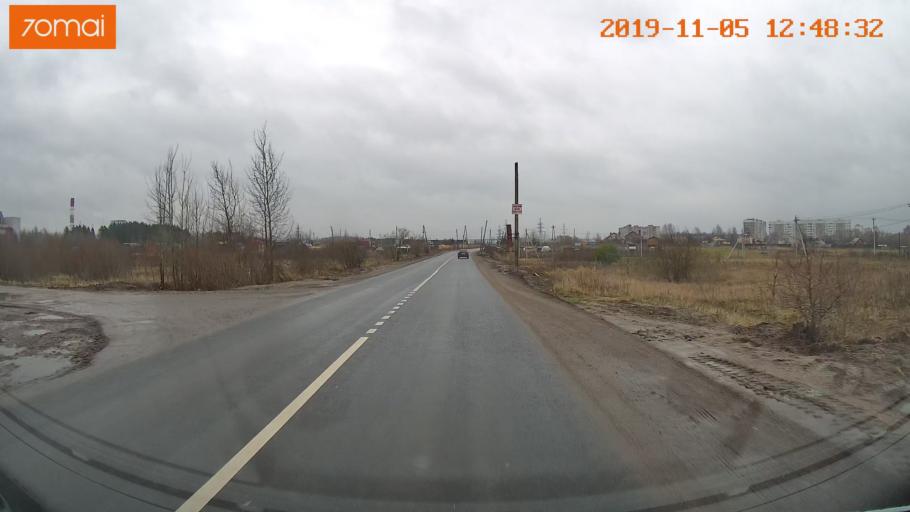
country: RU
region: Ivanovo
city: Kokhma
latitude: 56.9604
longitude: 41.0979
